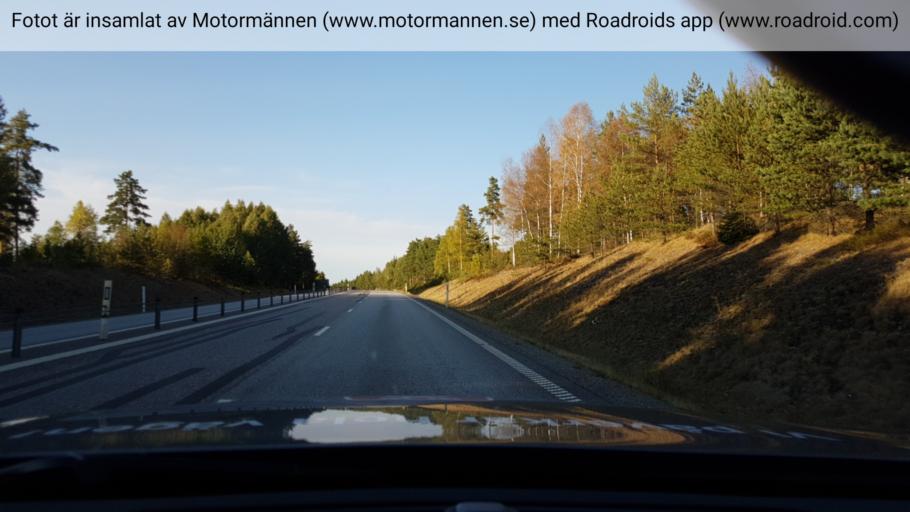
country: SE
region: OErebro
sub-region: Lindesbergs Kommun
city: Lindesberg
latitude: 59.5297
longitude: 15.1956
